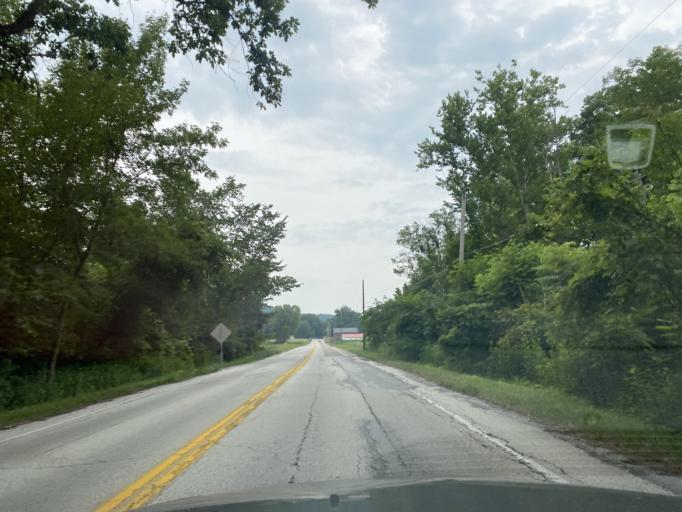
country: US
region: Ohio
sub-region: Summit County
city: Peninsula
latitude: 41.1968
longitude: -81.5753
